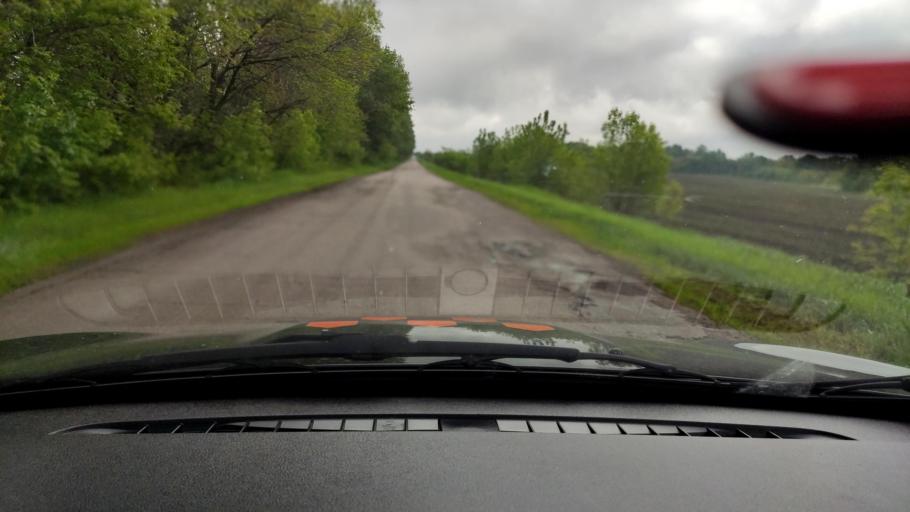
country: RU
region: Voronezj
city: Uryv-Pokrovka
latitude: 51.1275
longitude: 39.1108
